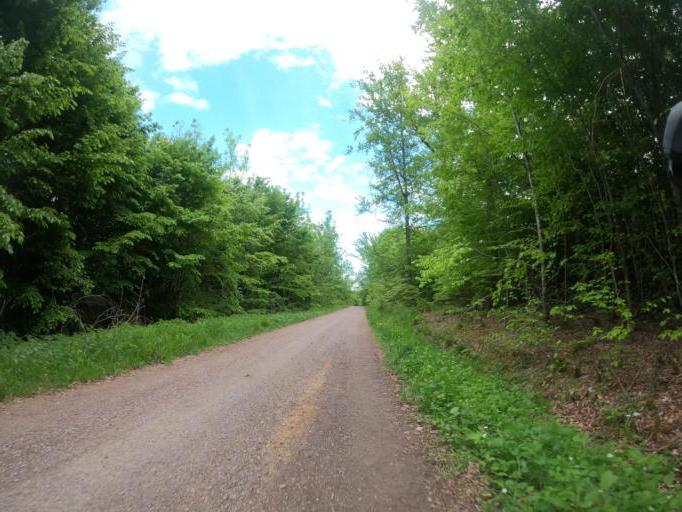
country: DE
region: Baden-Wuerttemberg
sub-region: Regierungsbezirk Stuttgart
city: Holzgerlingen
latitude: 48.6495
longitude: 9.0273
